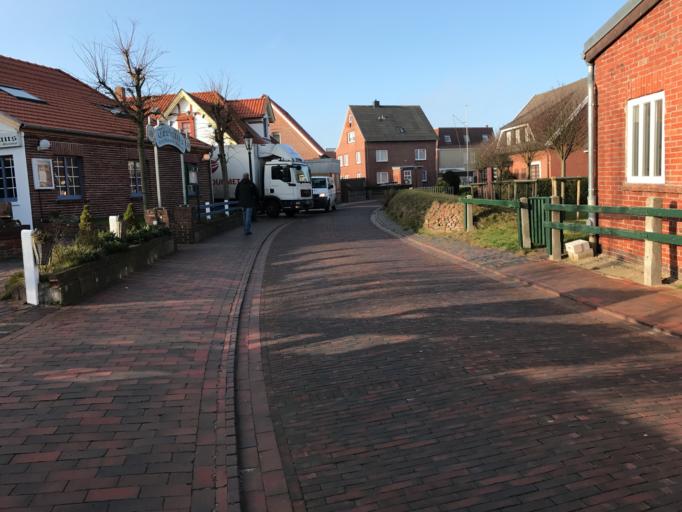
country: DE
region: Lower Saxony
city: Borkum
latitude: 53.5847
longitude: 6.6680
